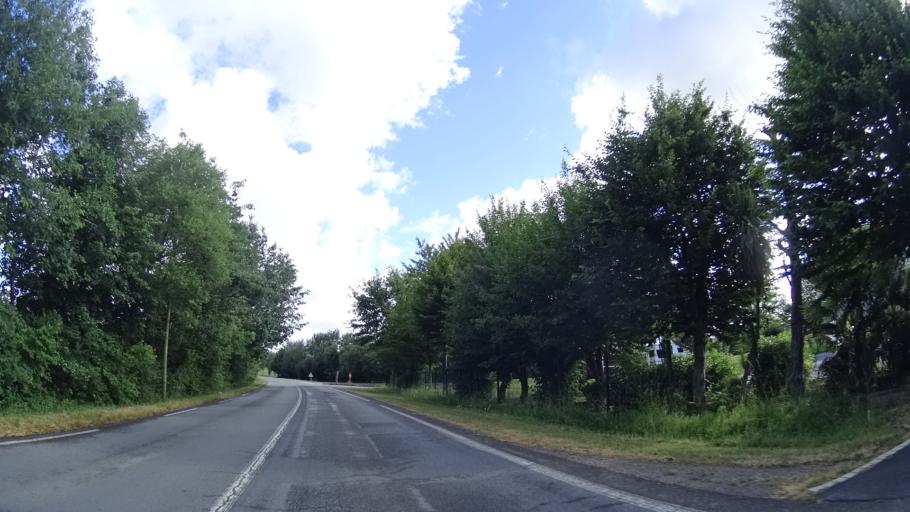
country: FR
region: Brittany
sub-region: Departement d'Ille-et-Vilaine
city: Vignoc
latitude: 48.2562
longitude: -1.7776
